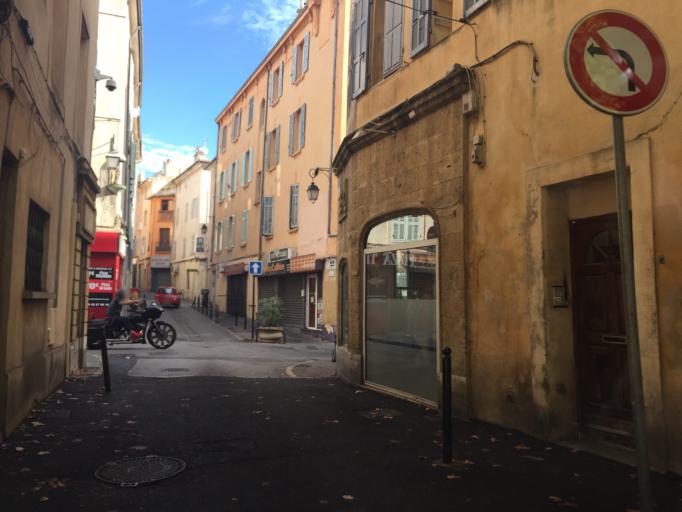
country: FR
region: Provence-Alpes-Cote d'Azur
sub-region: Departement des Bouches-du-Rhone
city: Aix-en-Provence
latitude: 43.5293
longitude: 5.4444
